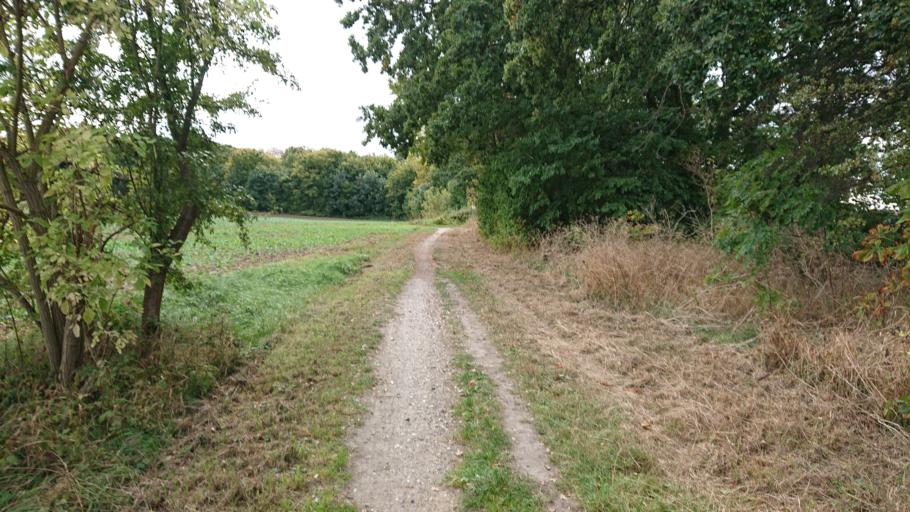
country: DE
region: Mecklenburg-Vorpommern
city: Altefahr
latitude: 54.3354
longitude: 13.1146
